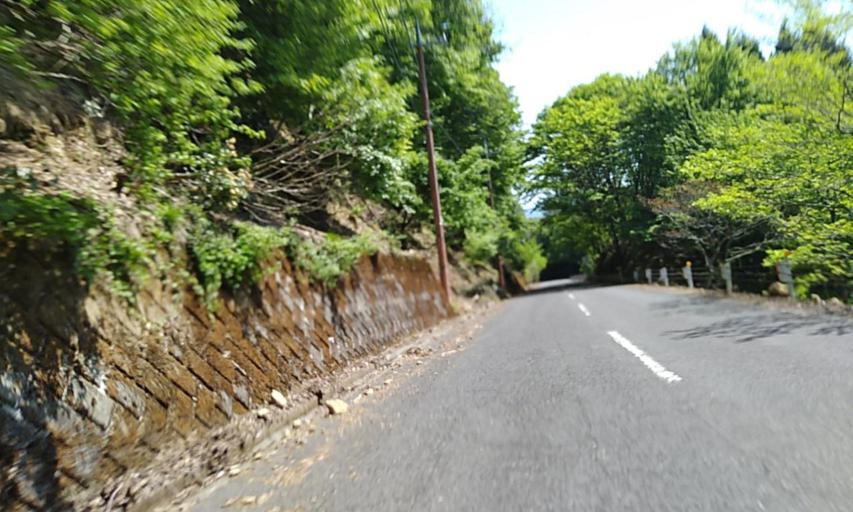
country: JP
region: Fukui
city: Obama
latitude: 35.5549
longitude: 135.7313
